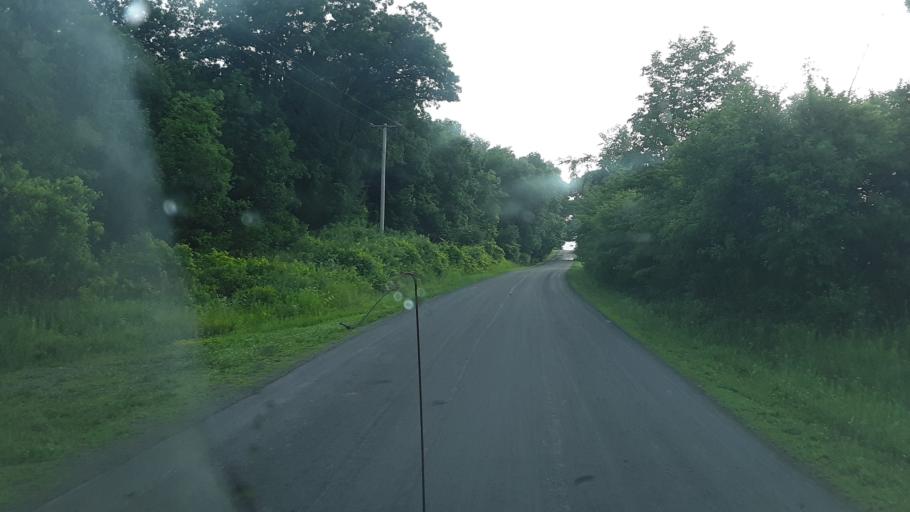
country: US
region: New York
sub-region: Montgomery County
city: Fonda
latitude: 42.9053
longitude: -74.3852
